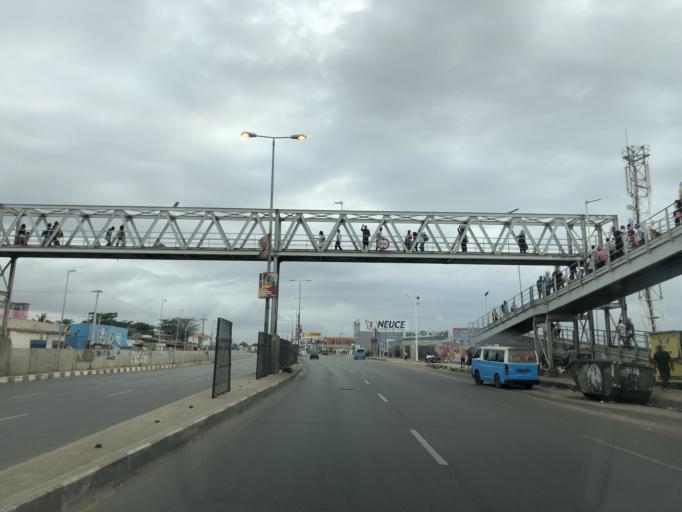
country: AO
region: Luanda
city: Luanda
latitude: -8.8615
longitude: 13.2152
